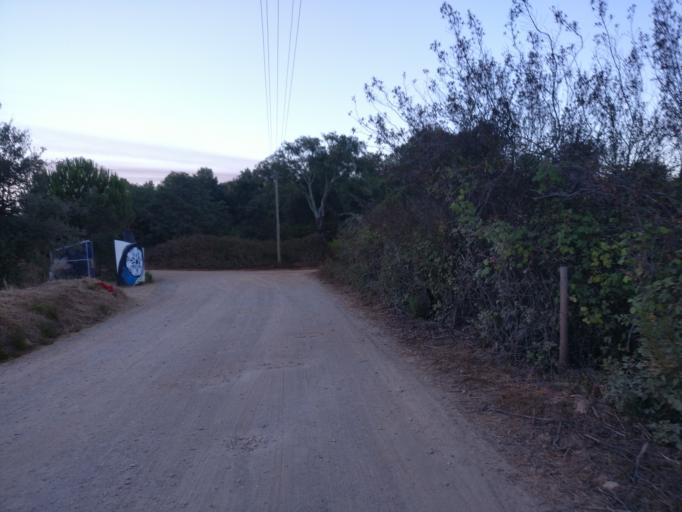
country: PT
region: Beja
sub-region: Odemira
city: Odemira
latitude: 37.7144
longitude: -8.5153
